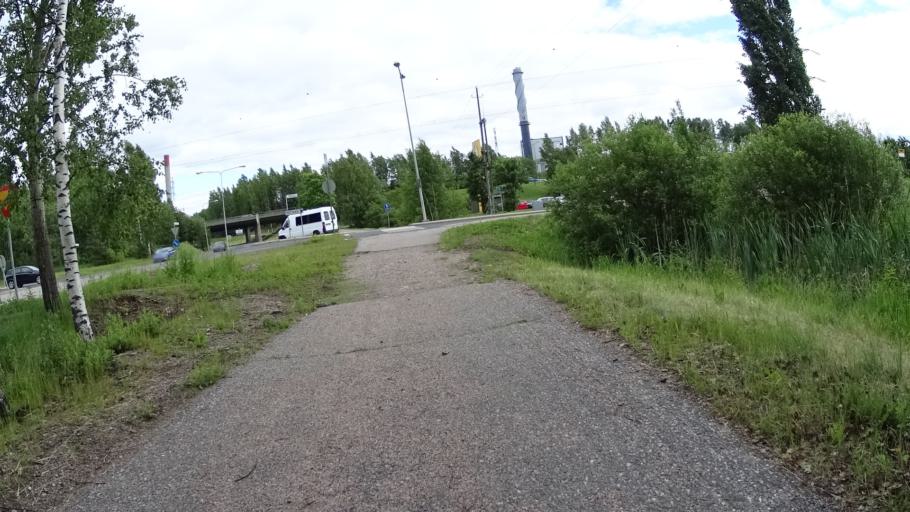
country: FI
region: Uusimaa
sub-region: Helsinki
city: Kilo
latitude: 60.2853
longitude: 24.8264
